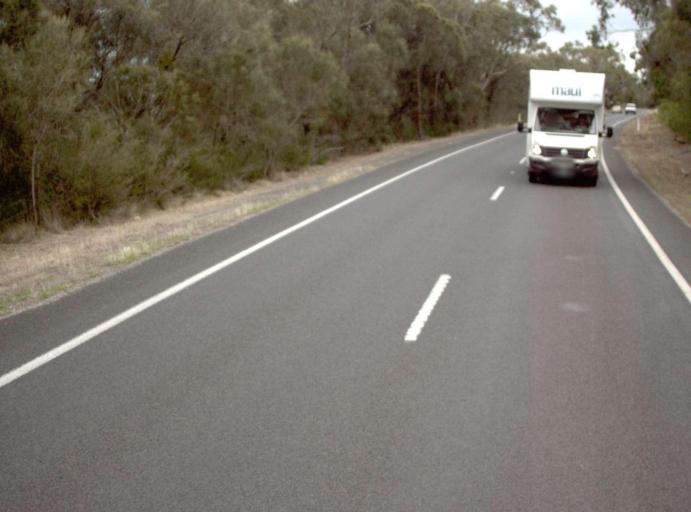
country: AU
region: Victoria
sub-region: Wellington
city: Sale
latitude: -38.2028
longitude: 147.0740
